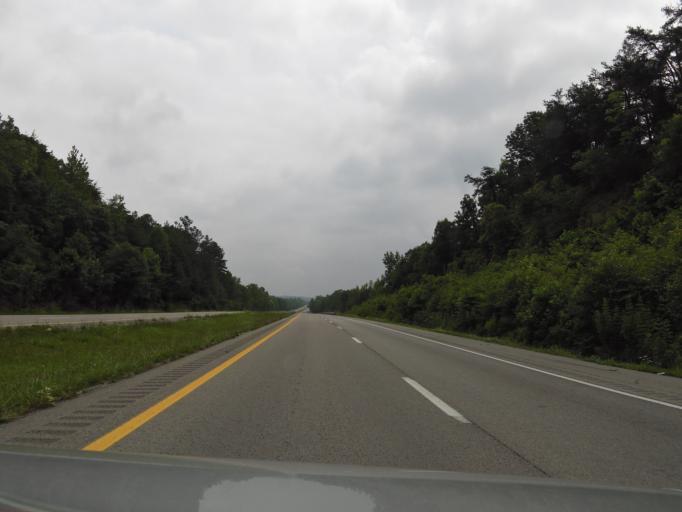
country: US
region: Kentucky
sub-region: Muhlenberg County
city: Central City
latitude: 37.3202
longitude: -87.0194
